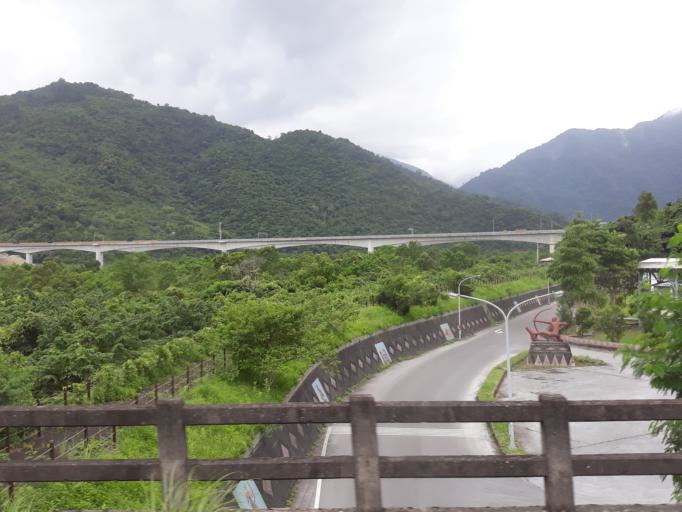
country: TW
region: Taiwan
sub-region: Yilan
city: Yilan
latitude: 24.4434
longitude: 121.7785
